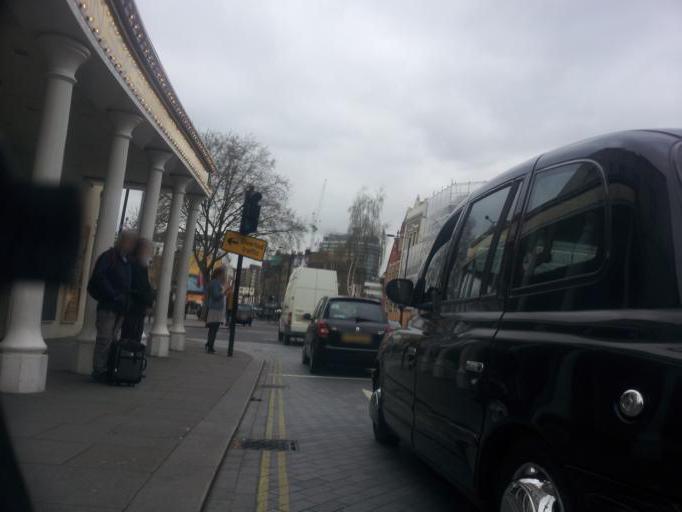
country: GB
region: England
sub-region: Greater London
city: Lambeth
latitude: 51.5025
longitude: -0.1094
